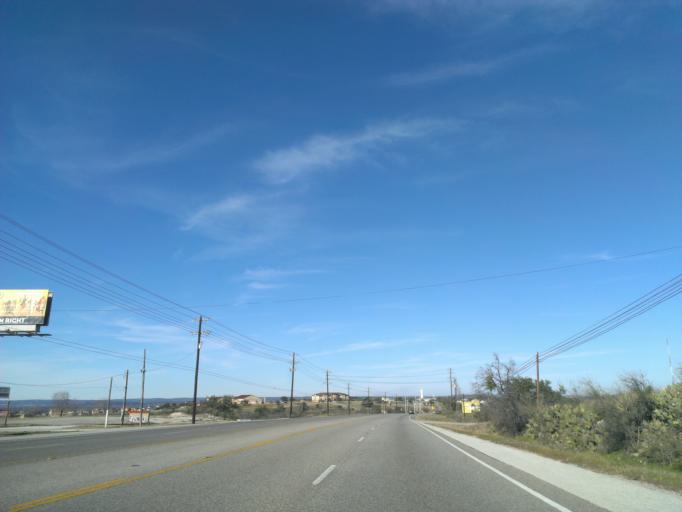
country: US
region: Texas
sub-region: Burnet County
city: Meadowlakes
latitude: 30.5476
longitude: -98.2764
